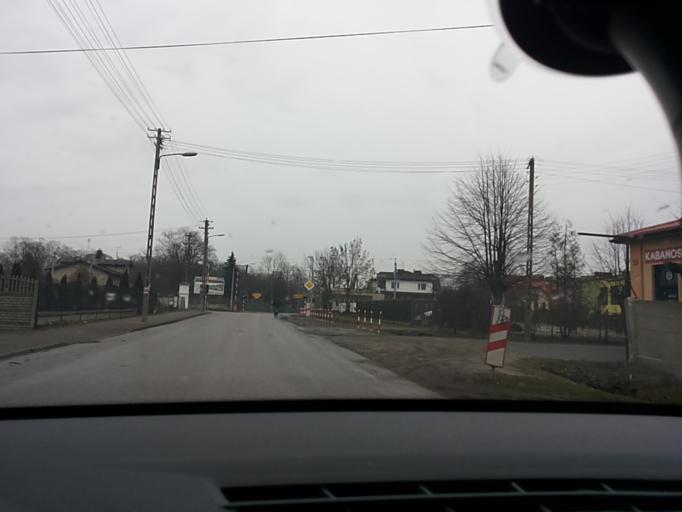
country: PL
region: Lodz Voivodeship
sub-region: Skierniewice
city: Skierniewice
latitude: 51.9616
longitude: 20.1336
